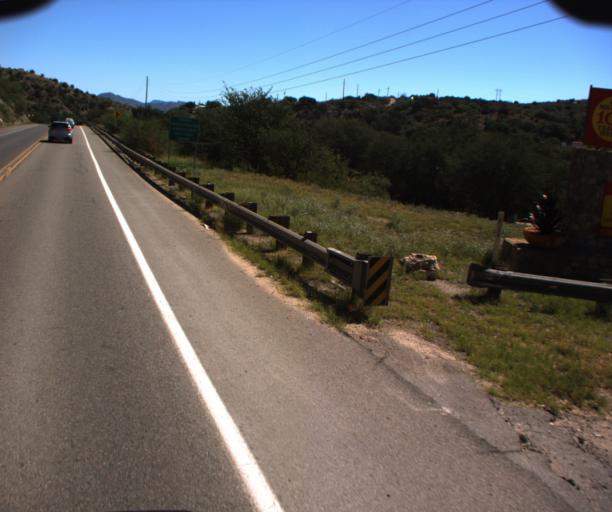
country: US
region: Arizona
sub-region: Gila County
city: Miami
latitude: 33.3861
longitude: -110.8891
